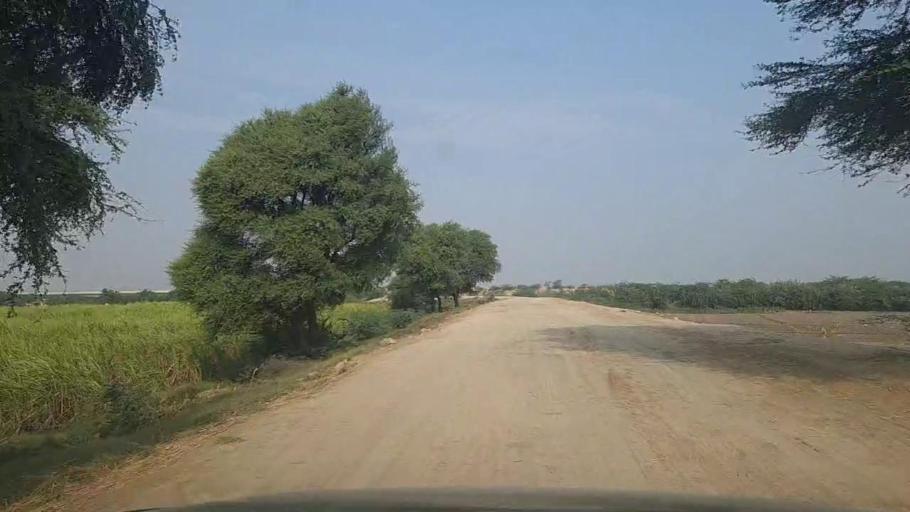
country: PK
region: Sindh
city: Bulri
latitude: 25.0313
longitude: 68.2799
